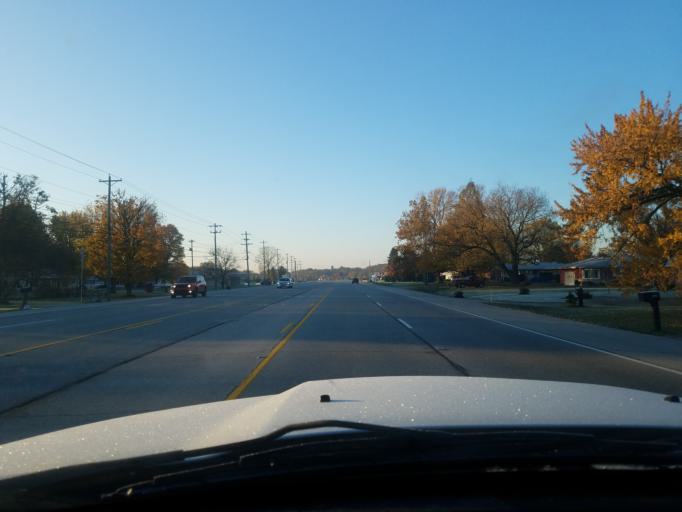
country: US
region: Indiana
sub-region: Montgomery County
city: Crawfordsville
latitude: 40.0699
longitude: -86.9071
